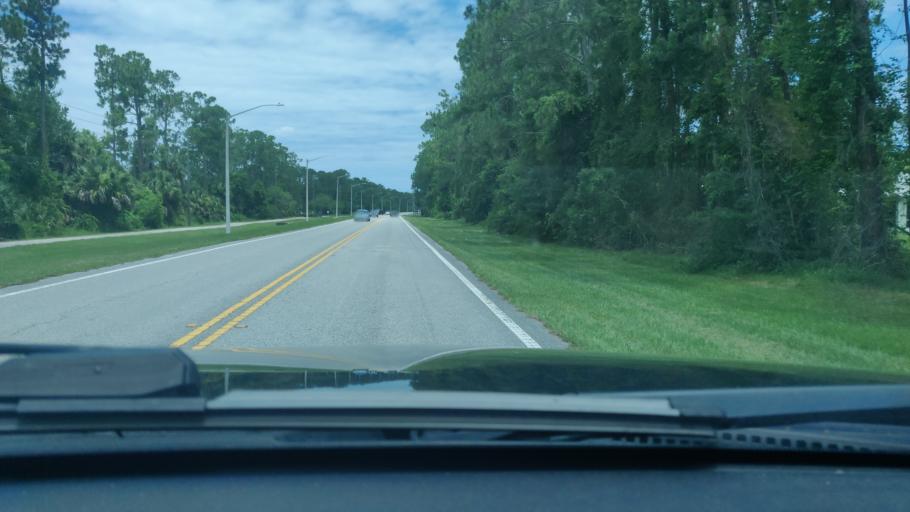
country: US
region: Florida
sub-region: Flagler County
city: Palm Coast
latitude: 29.5437
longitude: -81.2556
